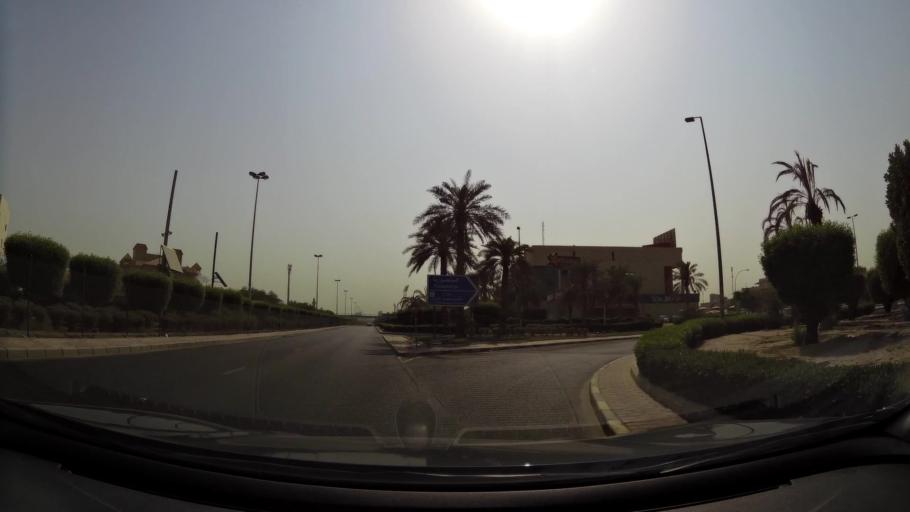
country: KW
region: Al Asimah
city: Ad Dasmah
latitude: 29.3615
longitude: 47.9967
